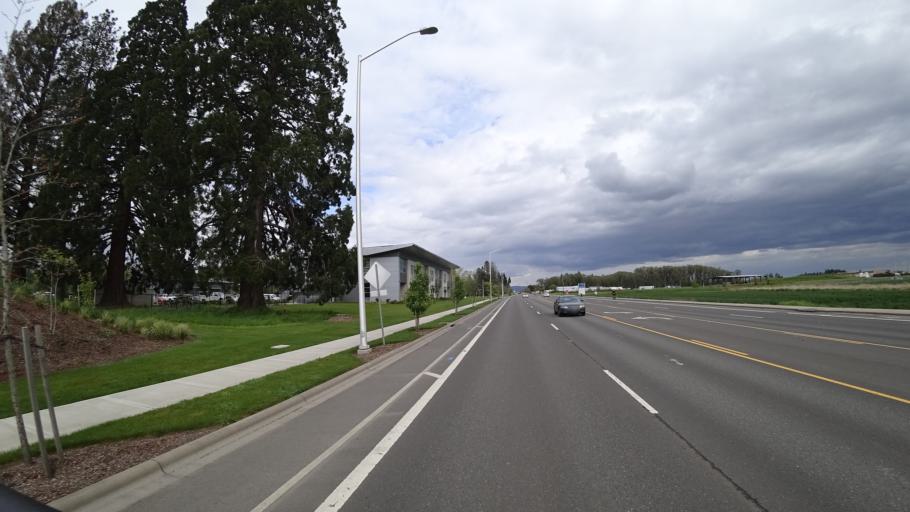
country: US
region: Oregon
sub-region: Washington County
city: Hillsboro
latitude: 45.5513
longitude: -122.9503
